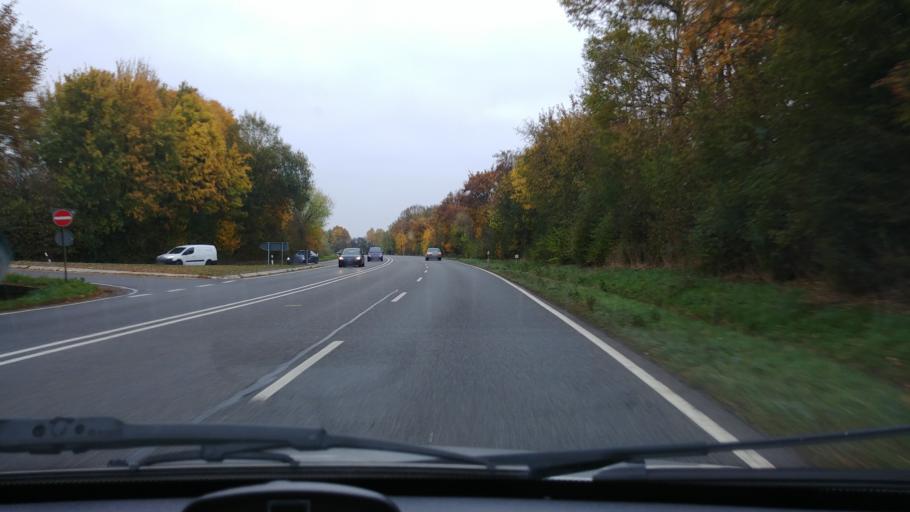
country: DE
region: Hesse
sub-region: Regierungsbezirk Giessen
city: Elz
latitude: 50.4627
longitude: 8.0597
